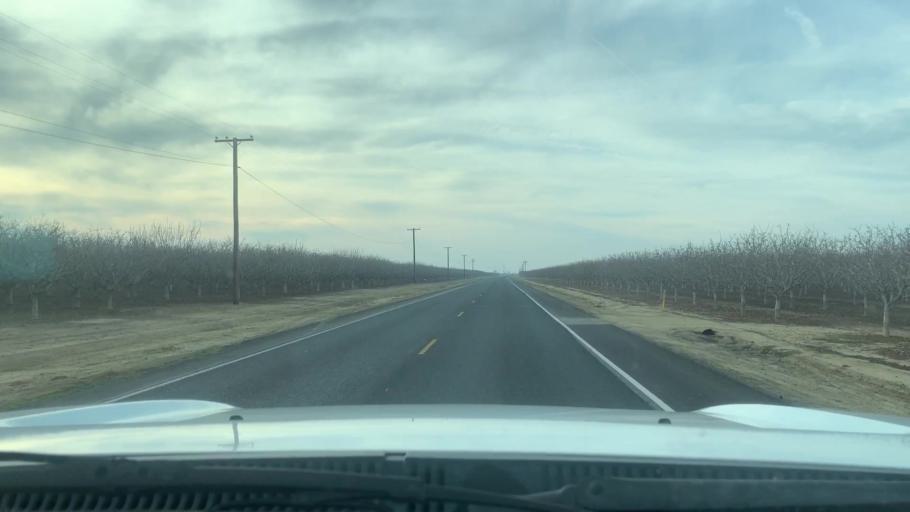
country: US
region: California
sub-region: Kern County
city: Lost Hills
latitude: 35.4993
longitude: -119.6317
